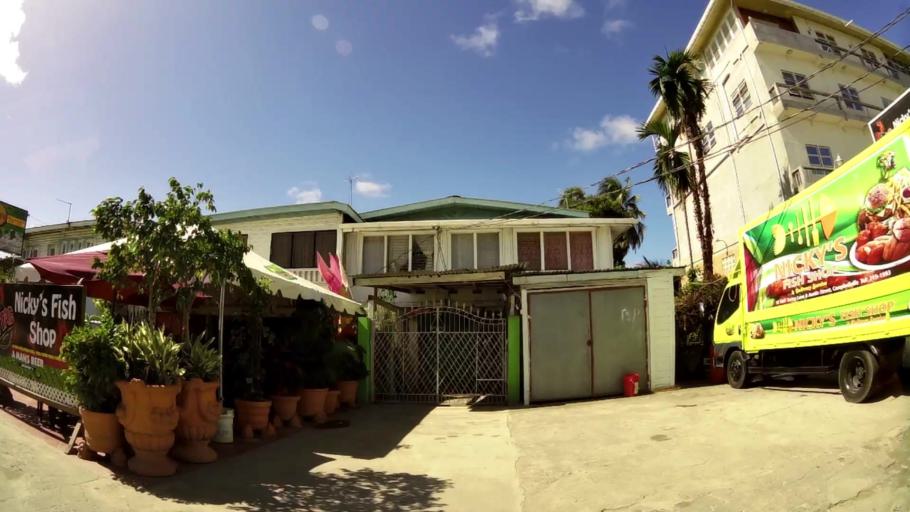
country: GY
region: Demerara-Mahaica
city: Georgetown
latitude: 6.8139
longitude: -58.1386
